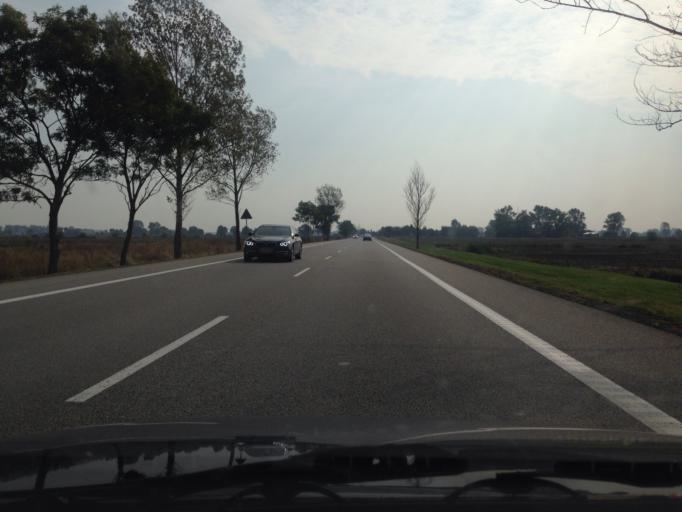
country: PL
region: Pomeranian Voivodeship
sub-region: Powiat nowodworski
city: Nowy Dwor Gdanski
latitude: 54.2301
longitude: 19.0488
